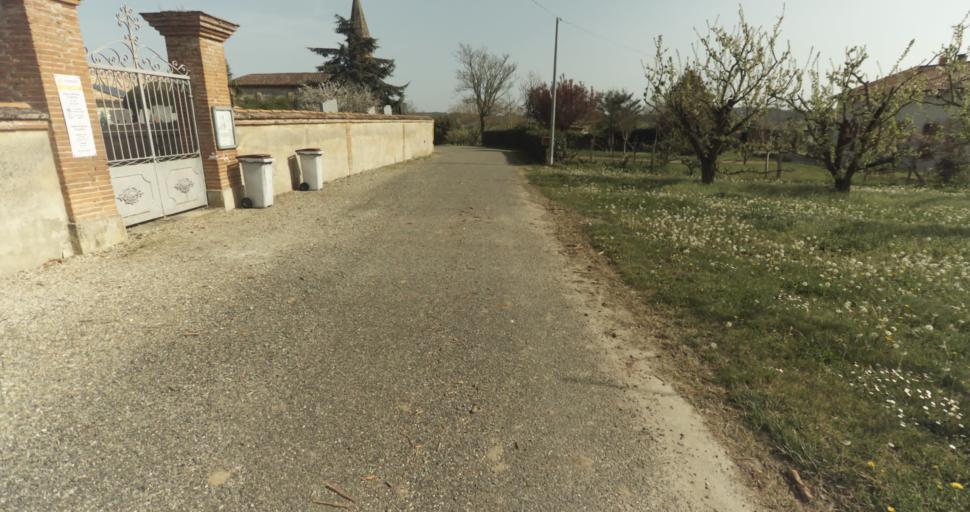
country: FR
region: Midi-Pyrenees
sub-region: Departement du Tarn-et-Garonne
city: Lafrancaise
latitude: 44.1432
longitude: 1.1721
